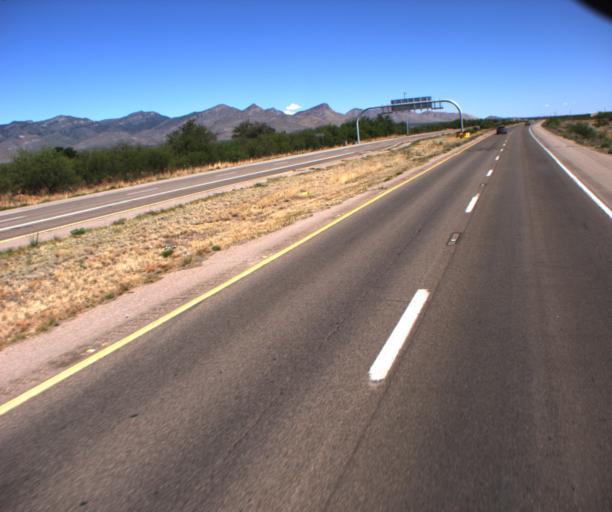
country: US
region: Arizona
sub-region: Cochise County
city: Huachuca City
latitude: 31.7199
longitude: -110.3502
